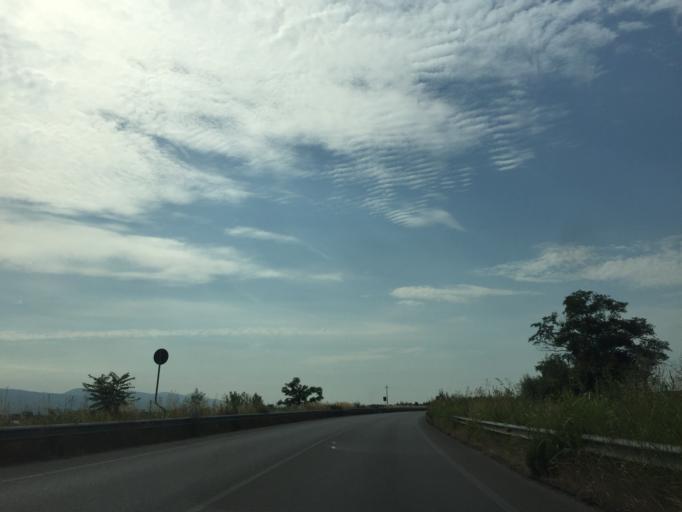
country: IT
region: Tuscany
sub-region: Provincia di Pistoia
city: Uggia-Pazzera-Bizzarrino
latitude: 43.8364
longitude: 10.8246
